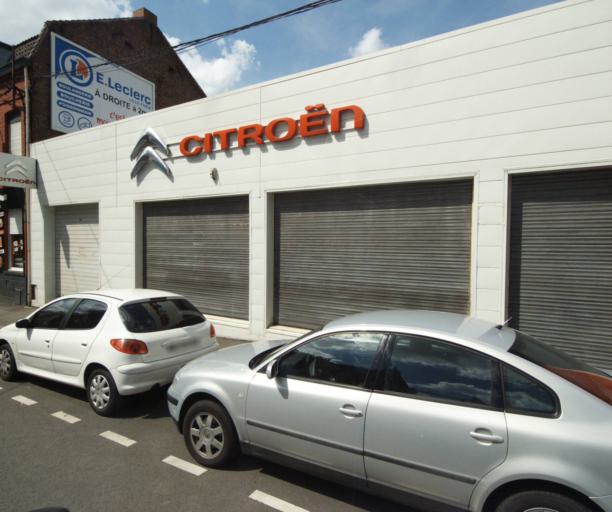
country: FR
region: Nord-Pas-de-Calais
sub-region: Departement du Nord
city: Mons-en-Baroeul
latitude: 50.6358
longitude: 3.1156
